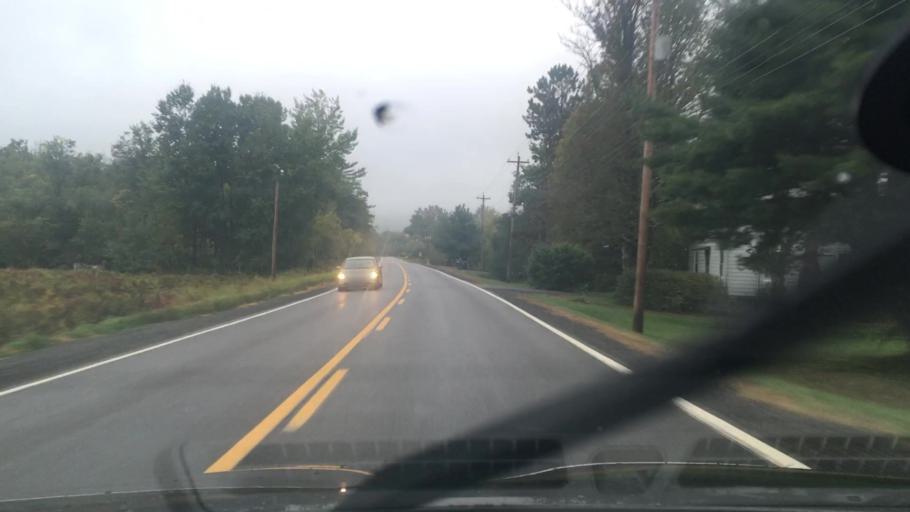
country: CA
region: Nova Scotia
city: Windsor
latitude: 44.9368
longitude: -64.1932
